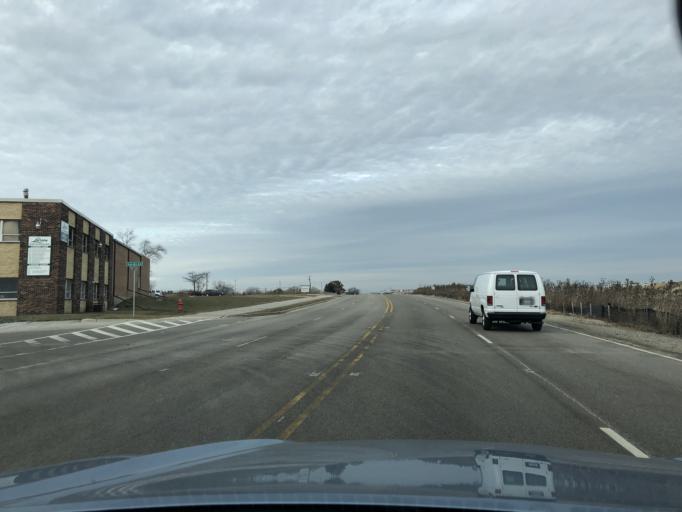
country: US
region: Illinois
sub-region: DuPage County
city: Bensenville
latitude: 41.9798
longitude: -87.9461
